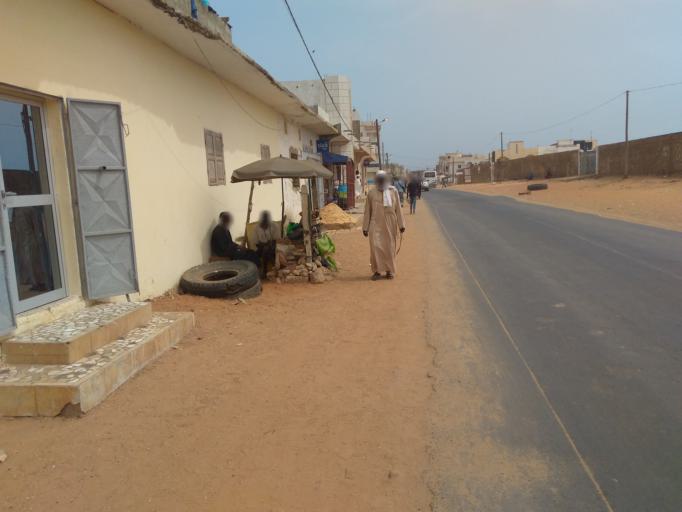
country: SN
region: Dakar
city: Pikine
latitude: 14.7996
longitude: -17.3372
